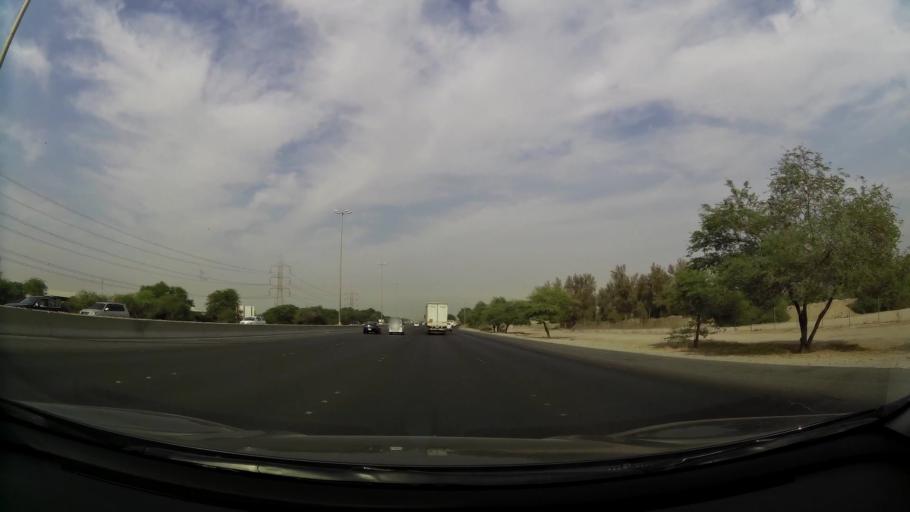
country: KW
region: Al Asimah
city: Ar Rabiyah
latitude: 29.2728
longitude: 47.8150
